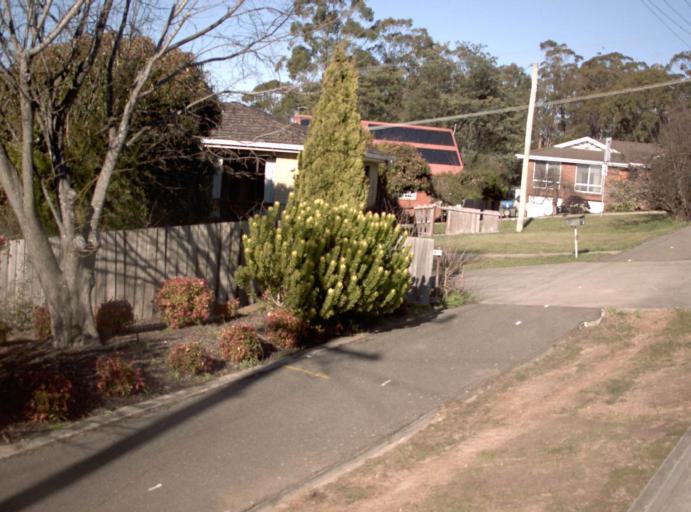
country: AU
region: Tasmania
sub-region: Launceston
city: Summerhill
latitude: -41.4741
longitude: 147.1324
